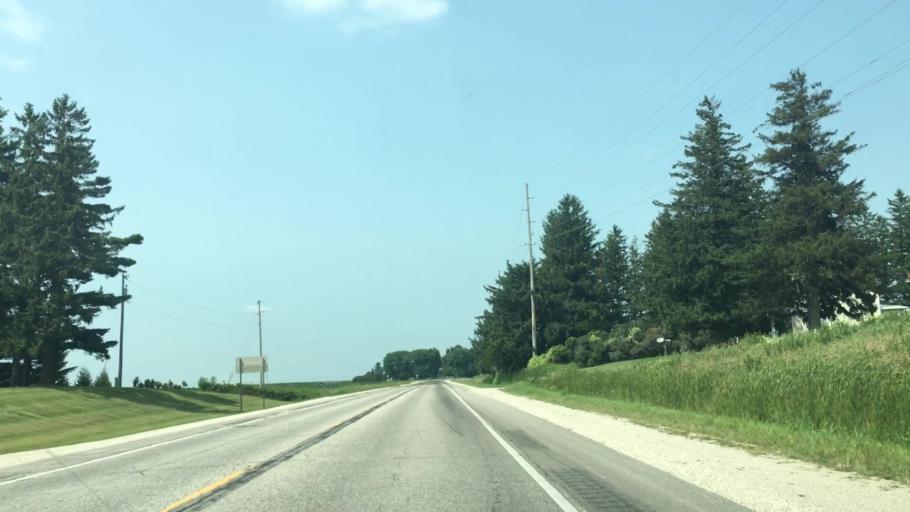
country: US
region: Iowa
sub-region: Fayette County
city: West Union
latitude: 42.9066
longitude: -91.8121
